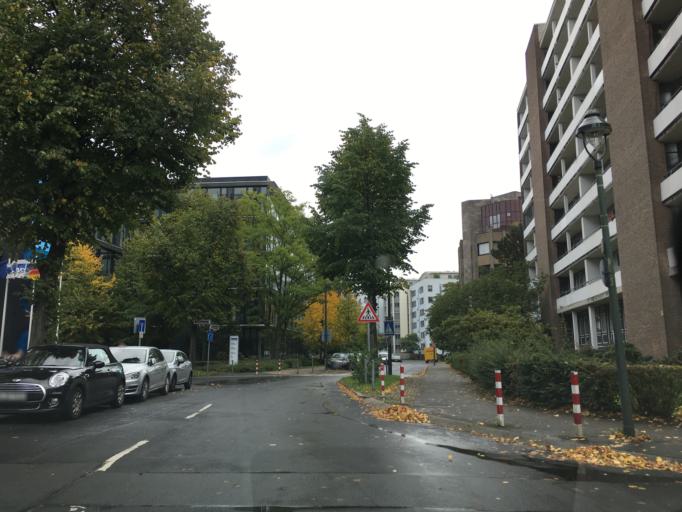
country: DE
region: North Rhine-Westphalia
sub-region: Regierungsbezirk Dusseldorf
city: Dusseldorf
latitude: 51.2525
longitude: 6.7637
